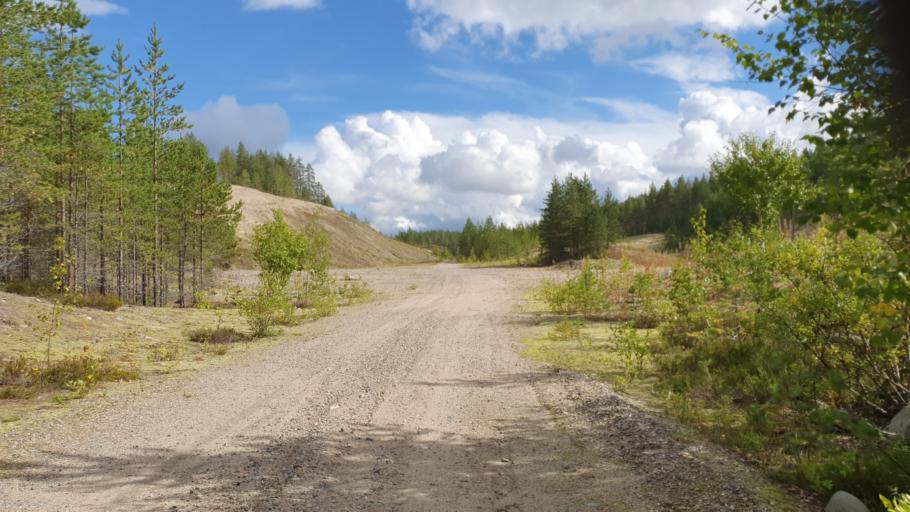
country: FI
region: Kainuu
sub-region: Kehys-Kainuu
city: Kuhmo
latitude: 64.1530
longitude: 29.3791
